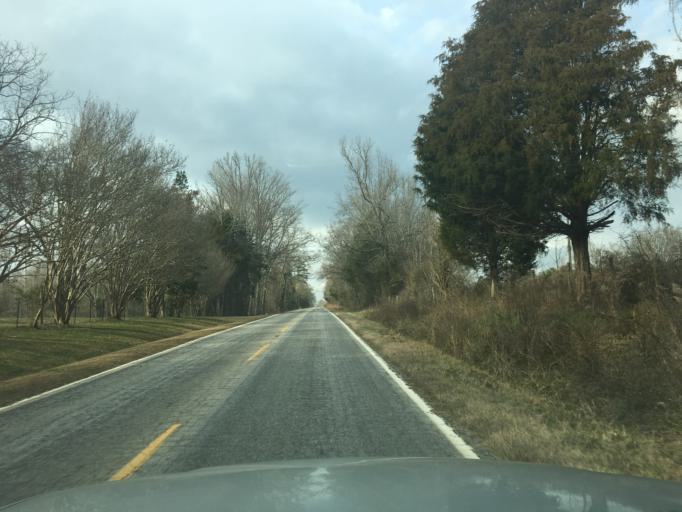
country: US
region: South Carolina
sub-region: Abbeville County
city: Due West
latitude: 34.2617
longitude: -82.4173
